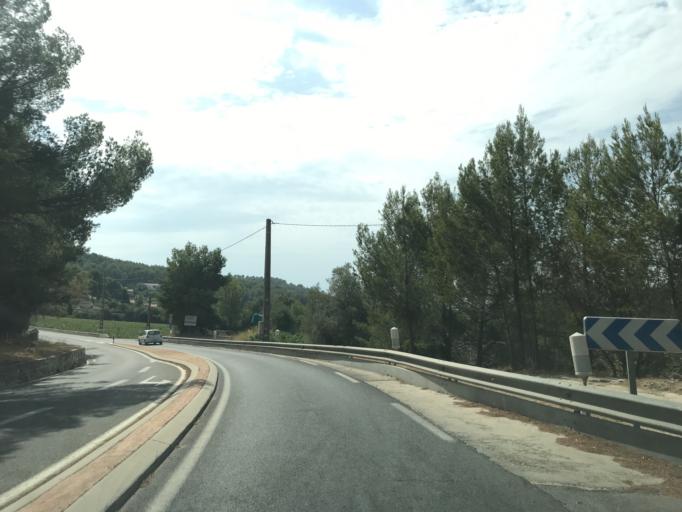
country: FR
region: Provence-Alpes-Cote d'Azur
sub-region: Departement du Var
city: Saint-Cyr-sur-Mer
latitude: 43.1658
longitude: 5.7158
